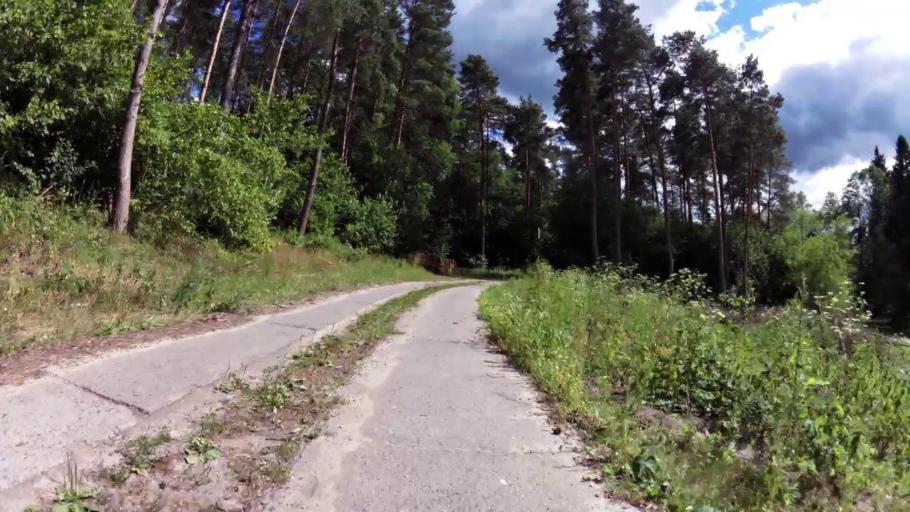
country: PL
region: West Pomeranian Voivodeship
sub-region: Powiat lobeski
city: Lobez
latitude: 53.6470
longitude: 15.5812
